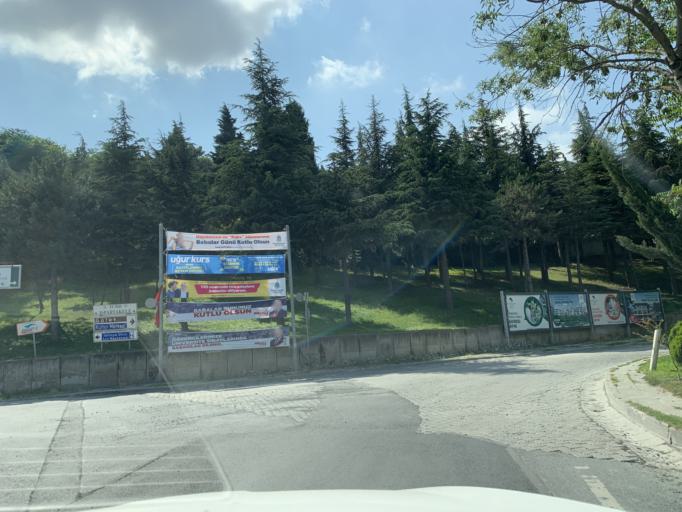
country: TR
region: Istanbul
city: Esenyurt
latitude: 41.0604
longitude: 28.6970
